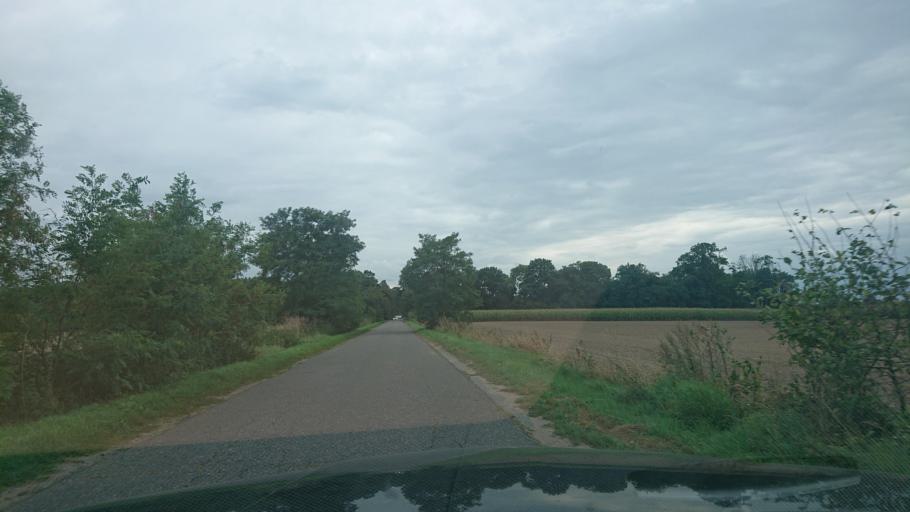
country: PL
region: Greater Poland Voivodeship
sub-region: Powiat gnieznienski
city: Niechanowo
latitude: 52.4596
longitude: 17.6199
